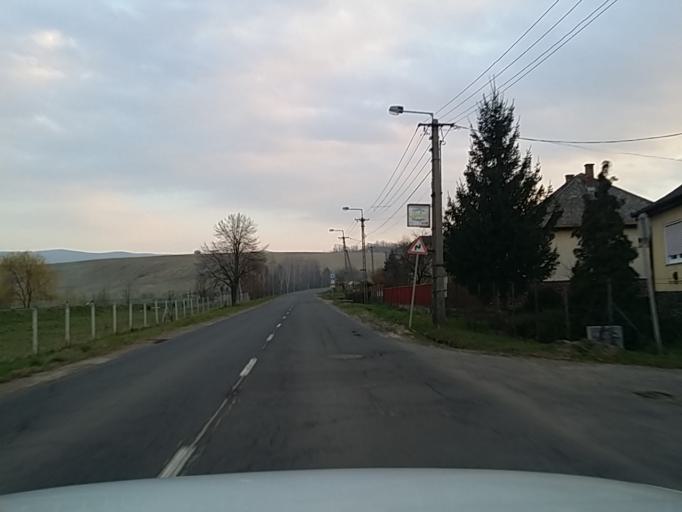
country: HU
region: Nograd
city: Batonyterenye
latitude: 47.9963
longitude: 19.8472
